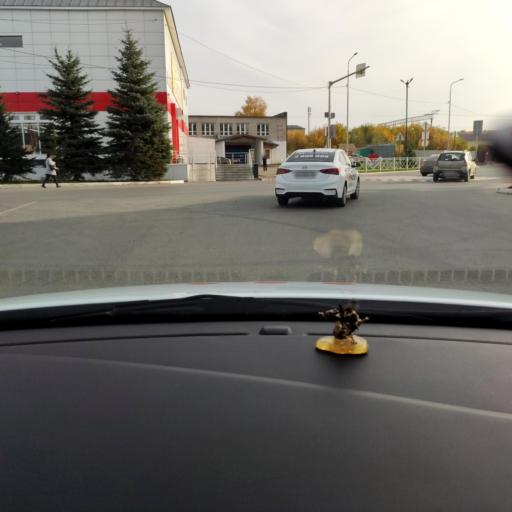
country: RU
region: Tatarstan
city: Vysokaya Gora
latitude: 55.9321
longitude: 49.3053
